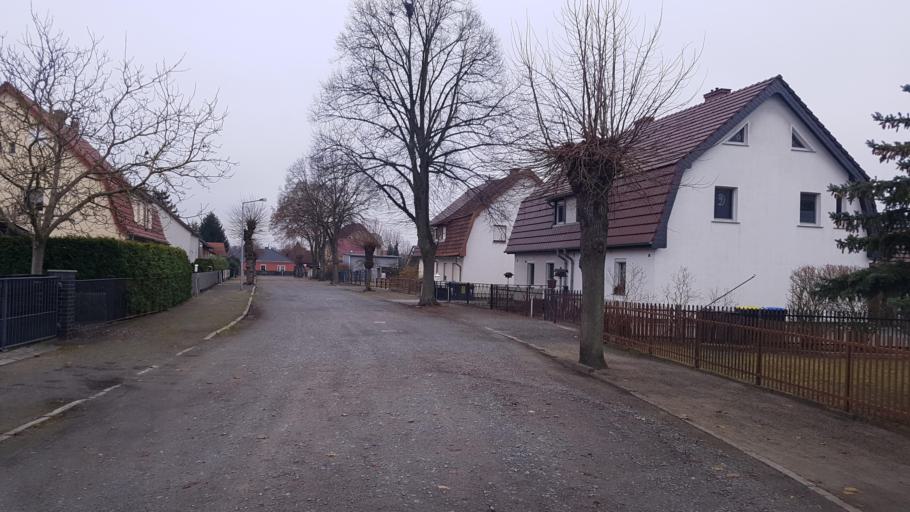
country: DE
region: Brandenburg
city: Lauchhammer
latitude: 51.4711
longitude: 13.7858
